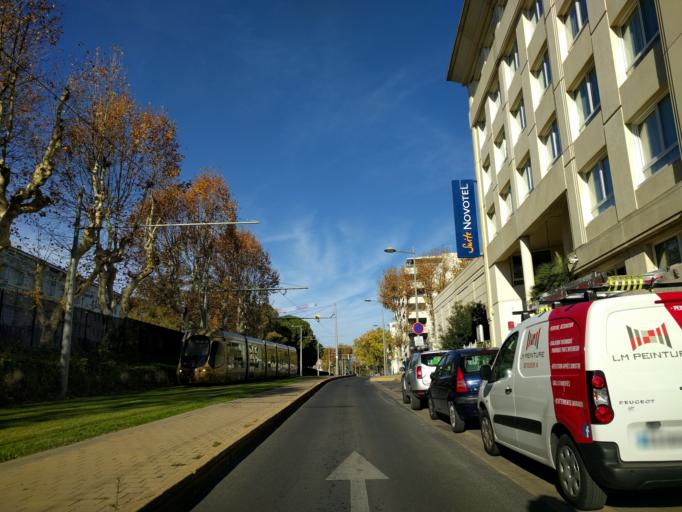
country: FR
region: Languedoc-Roussillon
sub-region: Departement de l'Herault
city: Montpellier
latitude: 43.6098
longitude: 3.8945
